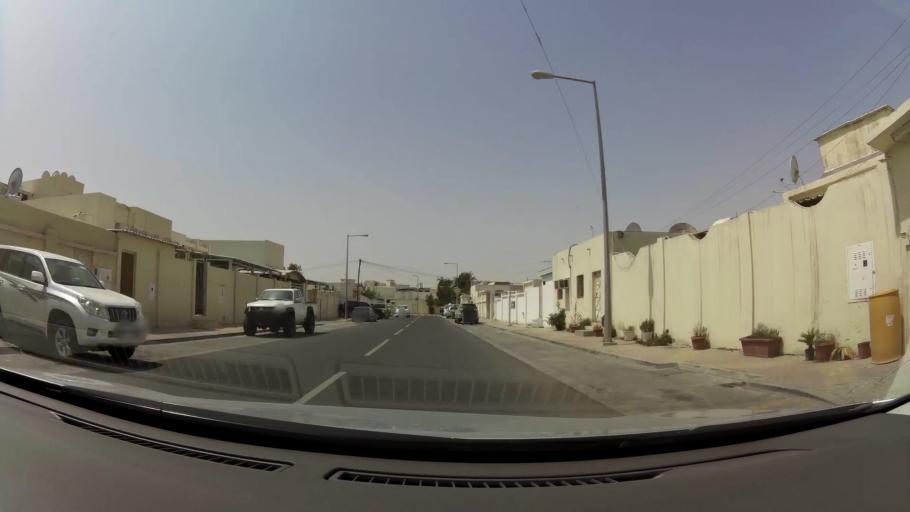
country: QA
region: Baladiyat ad Dawhah
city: Doha
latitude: 25.3202
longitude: 51.4795
